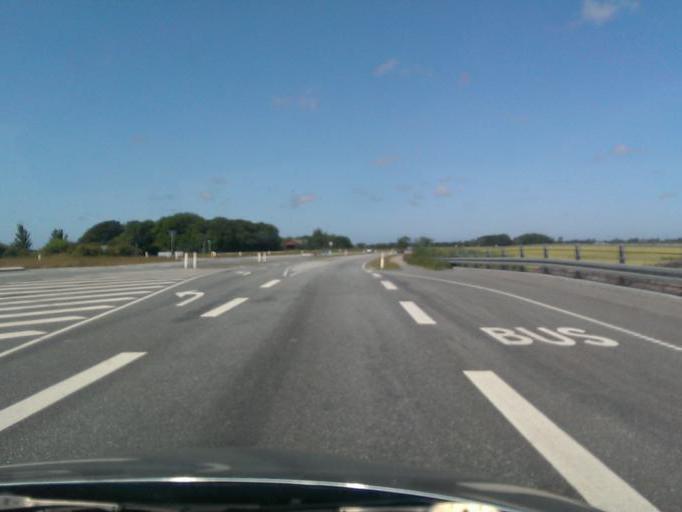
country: DK
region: North Denmark
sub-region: Jammerbugt Kommune
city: Abybro
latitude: 57.1688
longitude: 9.7169
